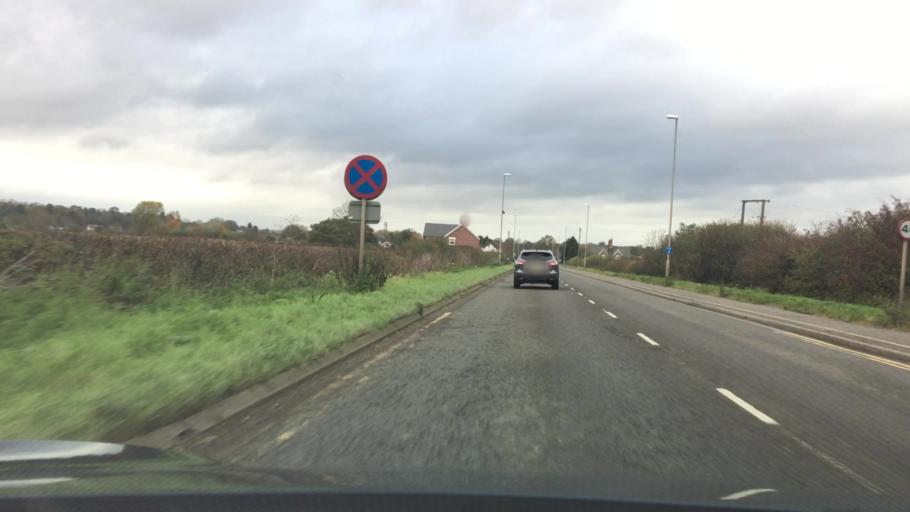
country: GB
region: England
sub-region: Nottinghamshire
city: Lowdham
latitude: 52.9988
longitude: -0.9951
